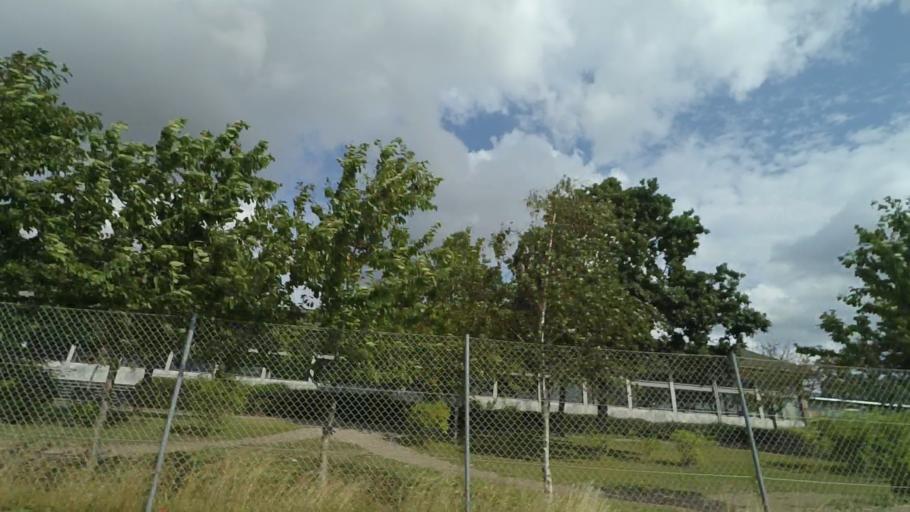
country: DK
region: Central Jutland
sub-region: Norddjurs Kommune
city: Auning
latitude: 56.4833
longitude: 10.4603
